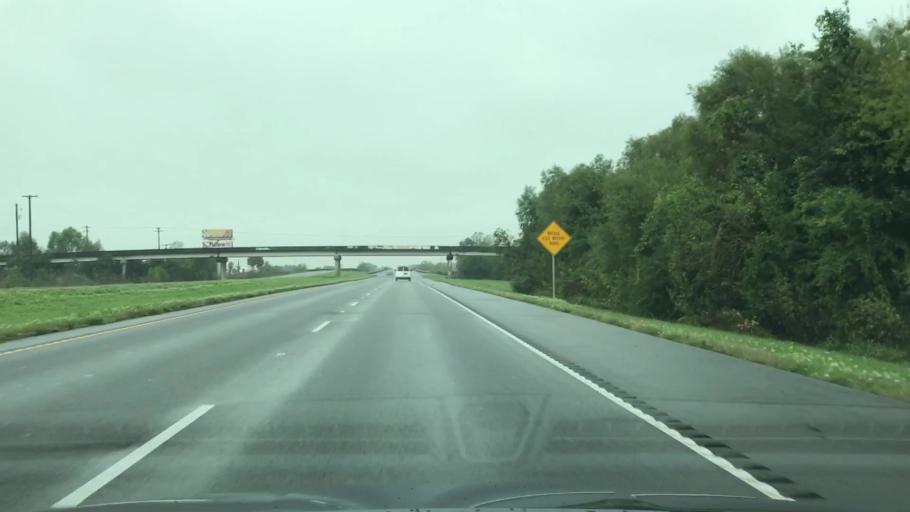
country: US
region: Louisiana
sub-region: Lafourche Parish
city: Raceland
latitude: 29.6903
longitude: -90.6005
